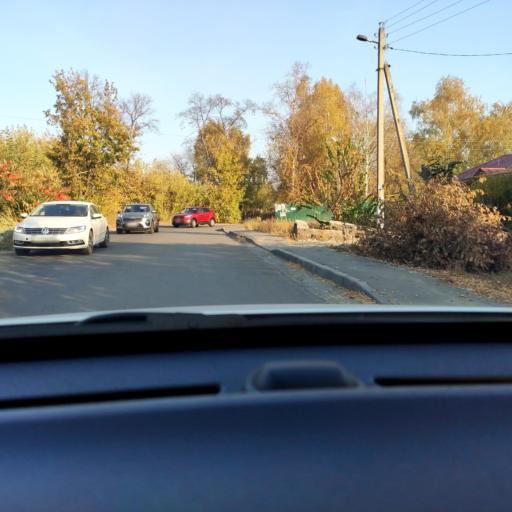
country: RU
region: Voronezj
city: Somovo
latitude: 51.6869
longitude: 39.3196
